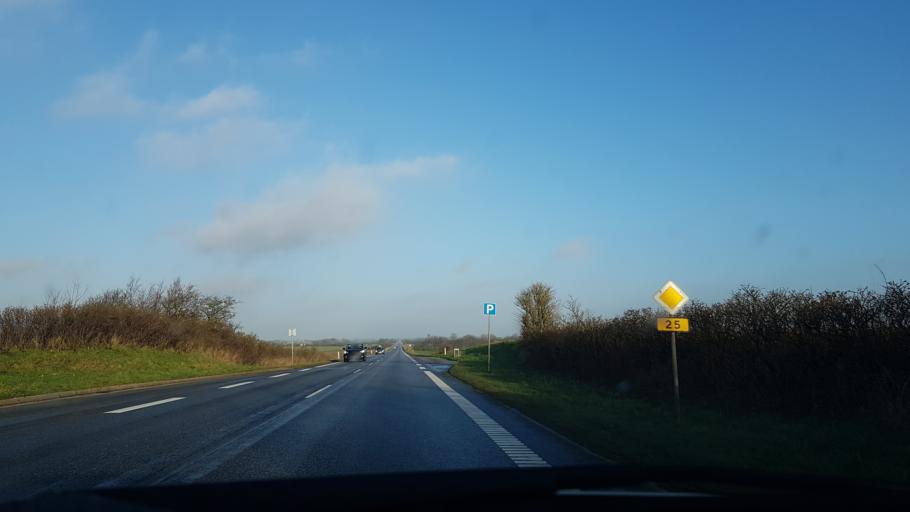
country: DK
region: South Denmark
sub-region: Tonder Kommune
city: Toftlund
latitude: 55.2143
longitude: 9.1003
